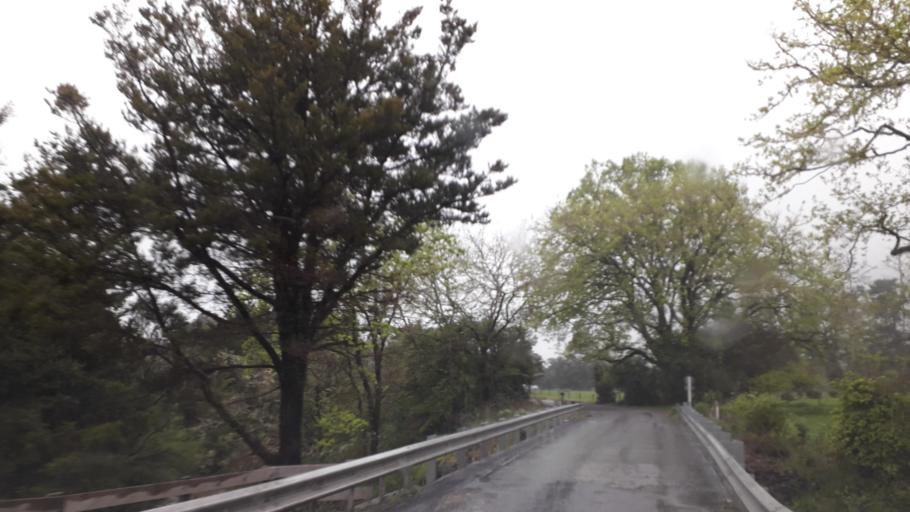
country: NZ
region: Northland
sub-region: Far North District
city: Waimate North
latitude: -35.4709
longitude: 173.6835
